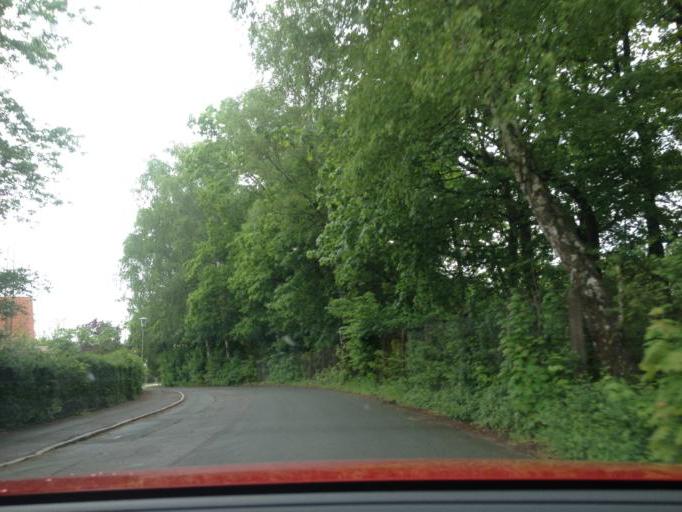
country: DE
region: Bavaria
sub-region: Regierungsbezirk Mittelfranken
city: Rothenbach an der Pegnitz
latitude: 49.4790
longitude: 11.2358
